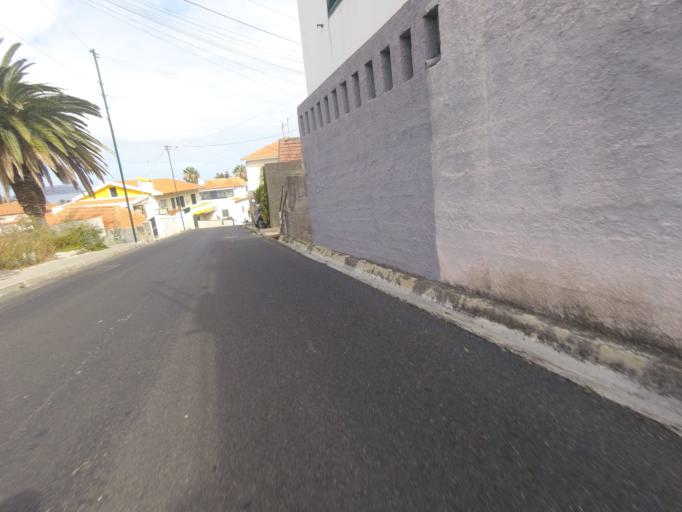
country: PT
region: Madeira
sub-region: Porto Santo
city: Vila de Porto Santo
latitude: 33.0575
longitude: -16.3397
